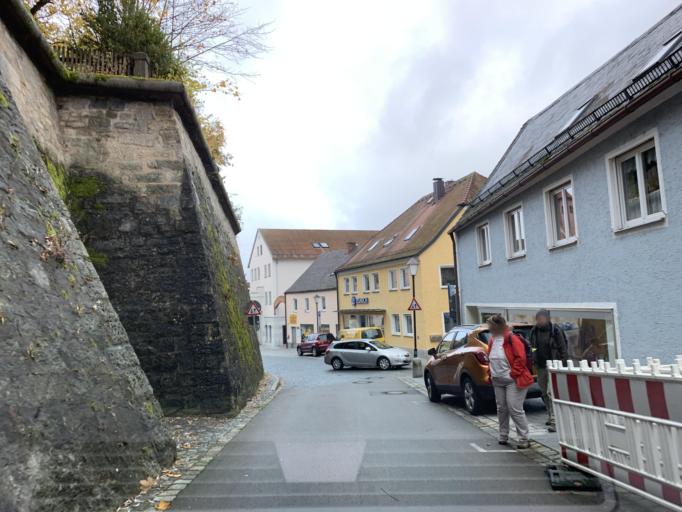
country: DE
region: Bavaria
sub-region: Upper Palatinate
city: Neunburg vorm Wald
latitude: 49.3493
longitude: 12.3840
